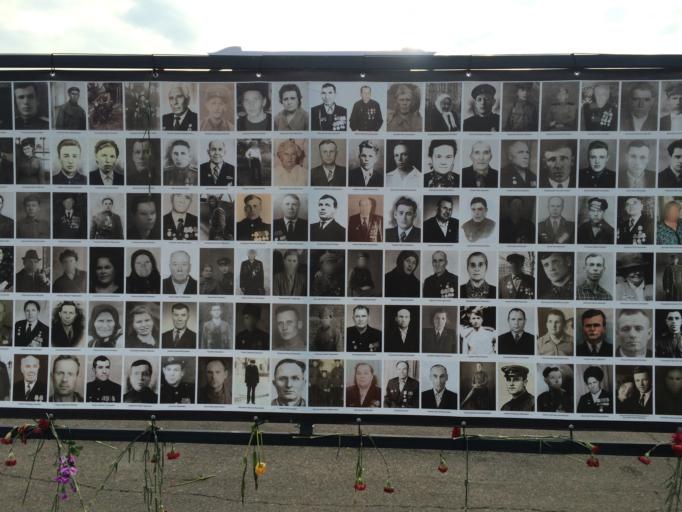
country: RU
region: Chelyabinsk
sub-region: Gorod Magnitogorsk
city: Magnitogorsk
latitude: 53.4077
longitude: 58.9913
